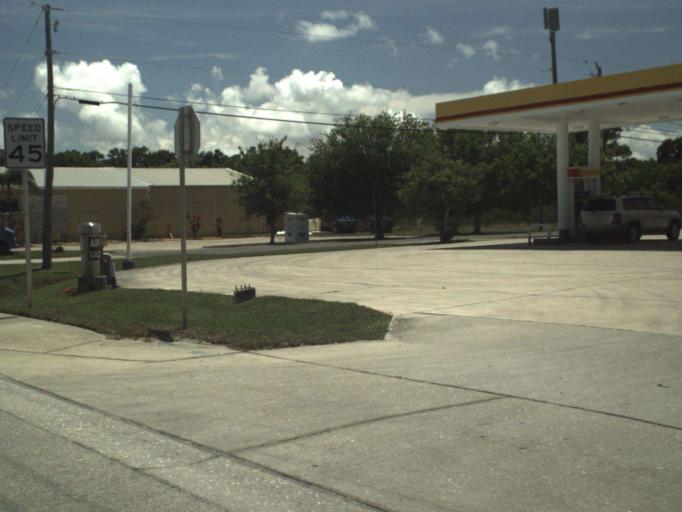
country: US
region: Florida
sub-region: Saint Lucie County
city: White City
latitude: 27.3623
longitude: -80.3260
